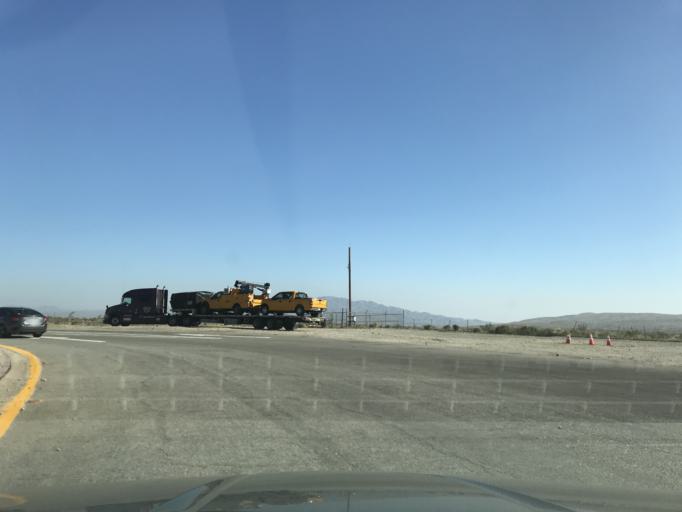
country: US
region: California
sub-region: Riverside County
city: Mecca
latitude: 33.6777
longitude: -115.9642
